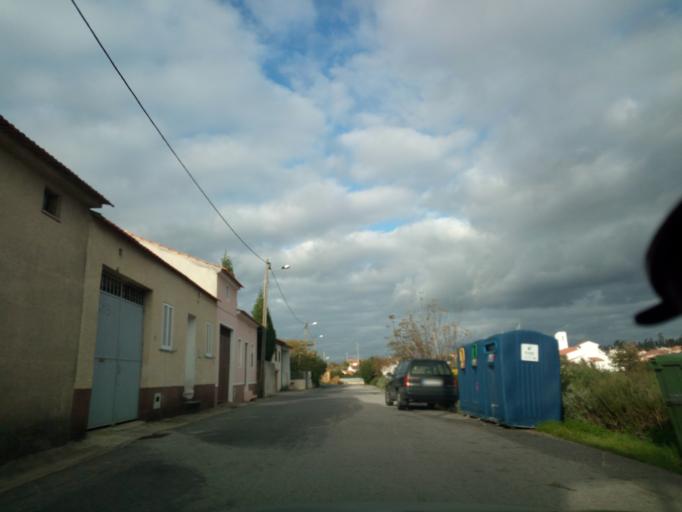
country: PT
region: Aveiro
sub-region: Oliveira do Bairro
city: Oliveira do Bairro
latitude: 40.5444
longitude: -8.4882
